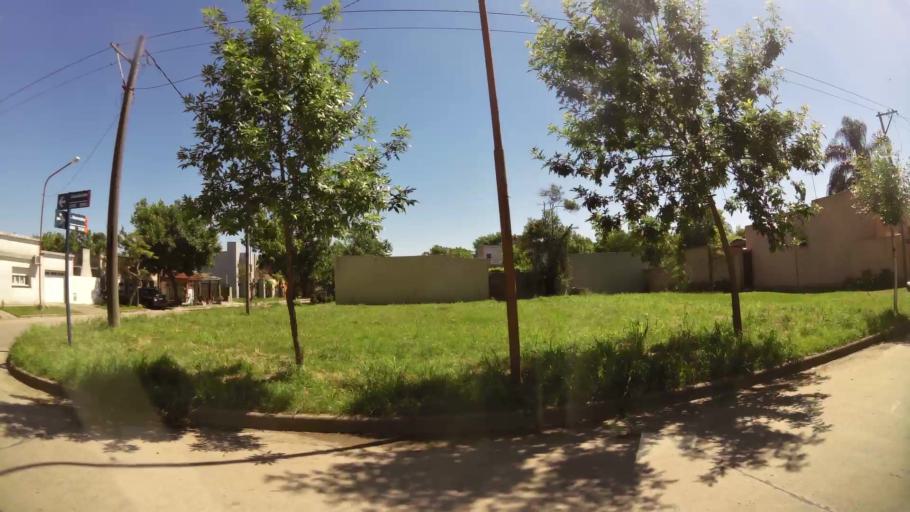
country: AR
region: Santa Fe
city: Esperanza
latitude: -31.4391
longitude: -60.9330
